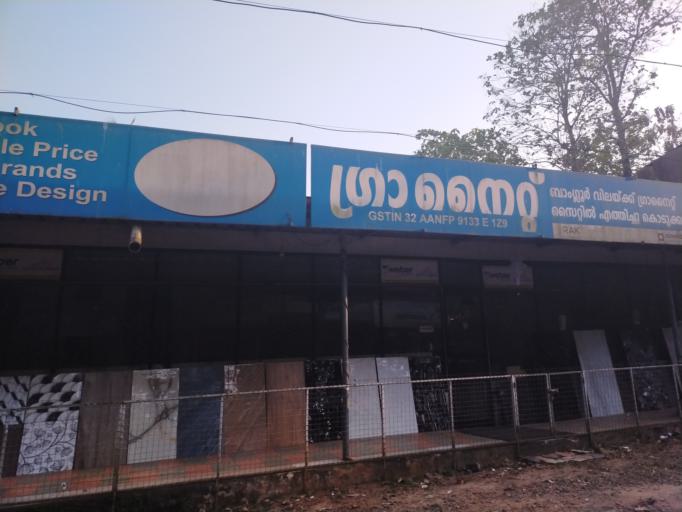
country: IN
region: Kerala
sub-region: Kottayam
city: Palackattumala
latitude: 9.7391
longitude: 76.5157
